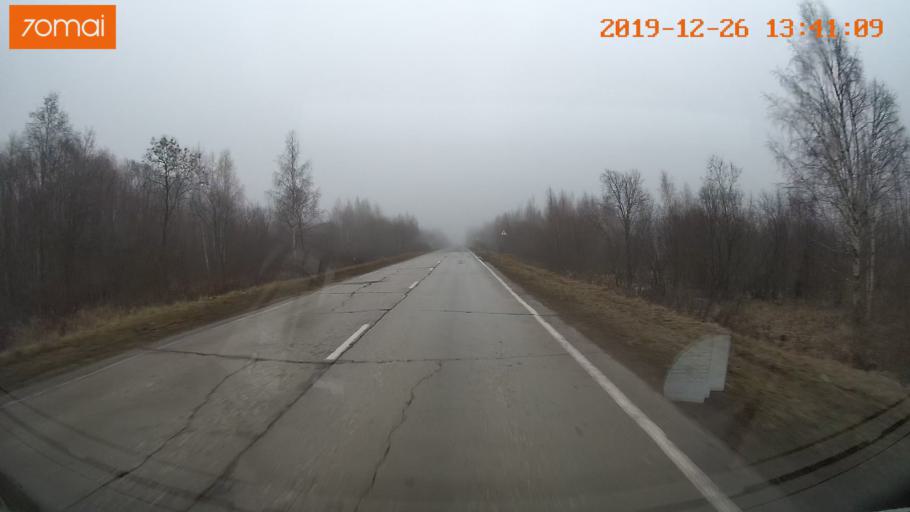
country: RU
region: Vologda
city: Sheksna
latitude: 58.7348
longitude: 38.4433
